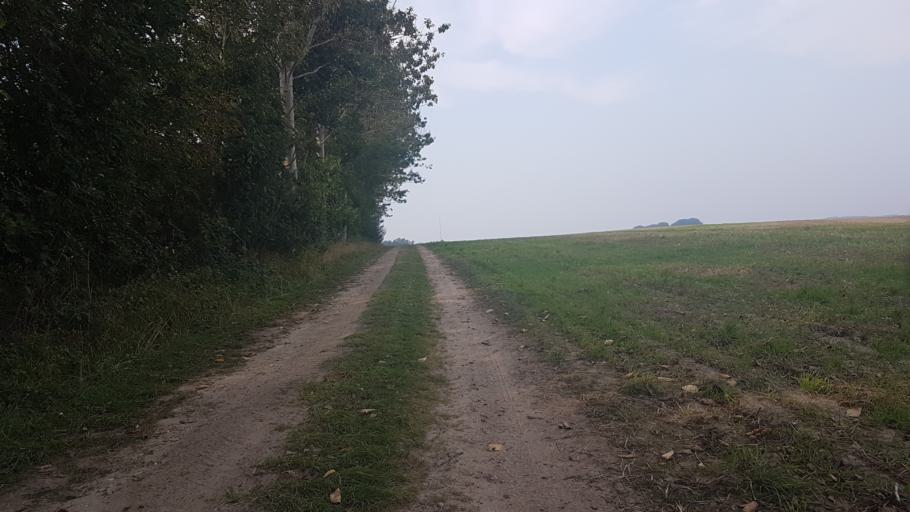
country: DE
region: Mecklenburg-Vorpommern
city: Garz
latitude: 54.2981
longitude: 13.3634
